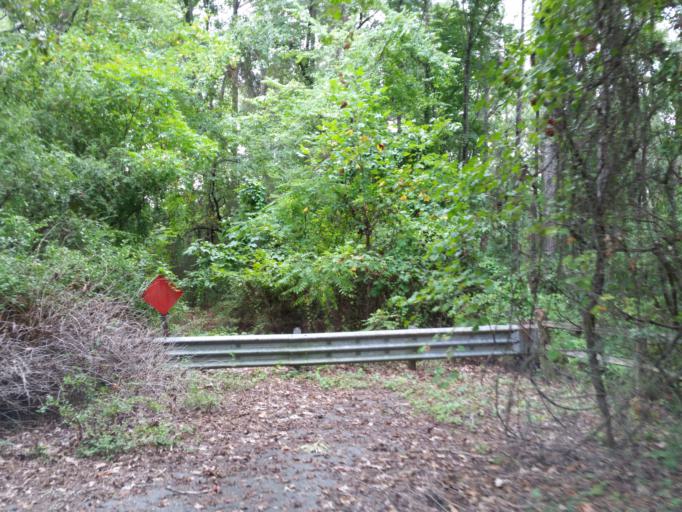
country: US
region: Georgia
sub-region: Cherokee County
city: Woodstock
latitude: 34.0286
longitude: -84.5298
